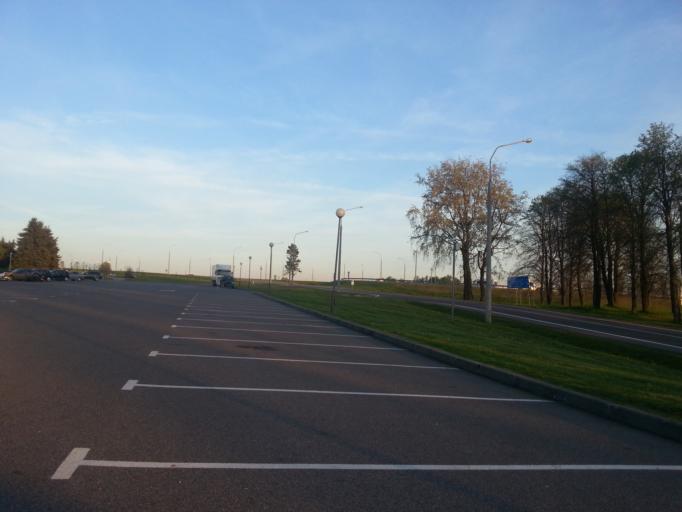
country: BY
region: Minsk
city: Slabada
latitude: 54.0189
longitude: 27.8919
